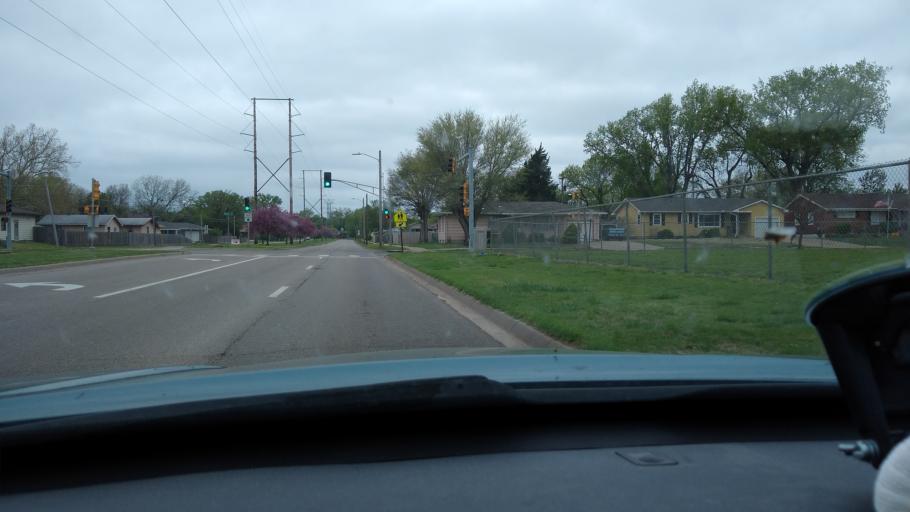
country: US
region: Kansas
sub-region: Saline County
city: Salina
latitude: 38.8034
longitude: -97.5980
